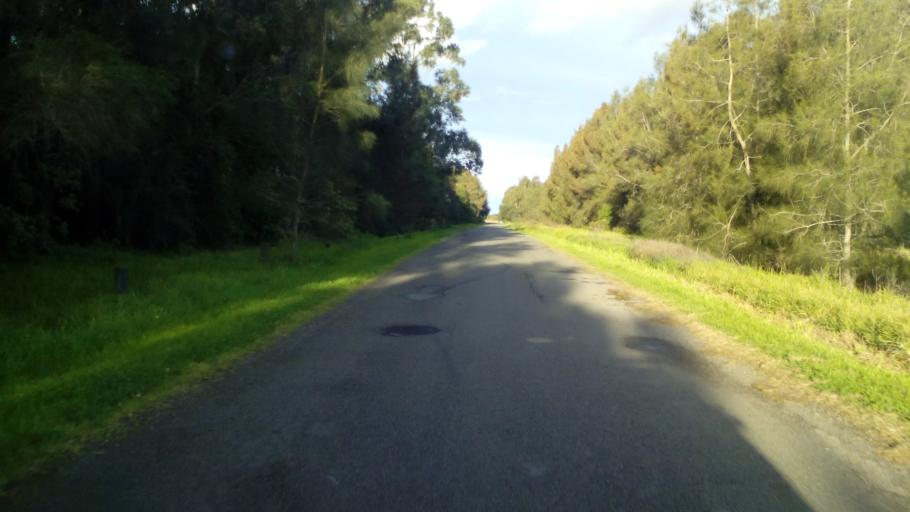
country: AU
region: New South Wales
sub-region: Newcastle
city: Mayfield West
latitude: -32.8408
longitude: 151.7109
